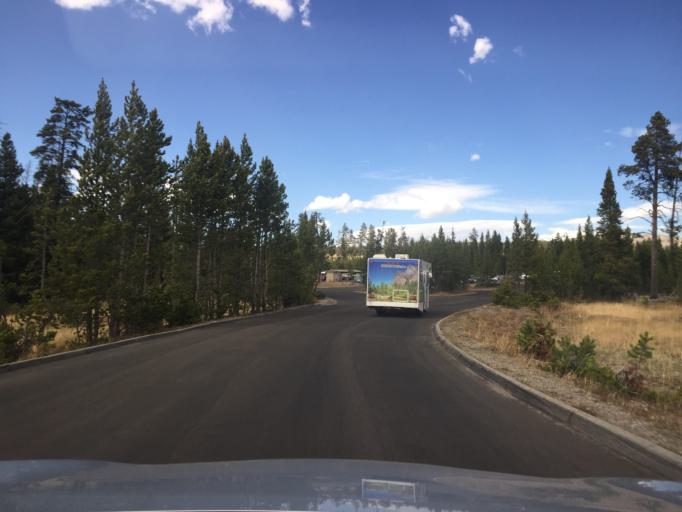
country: US
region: Montana
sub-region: Gallatin County
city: West Yellowstone
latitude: 44.7137
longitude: -110.4953
